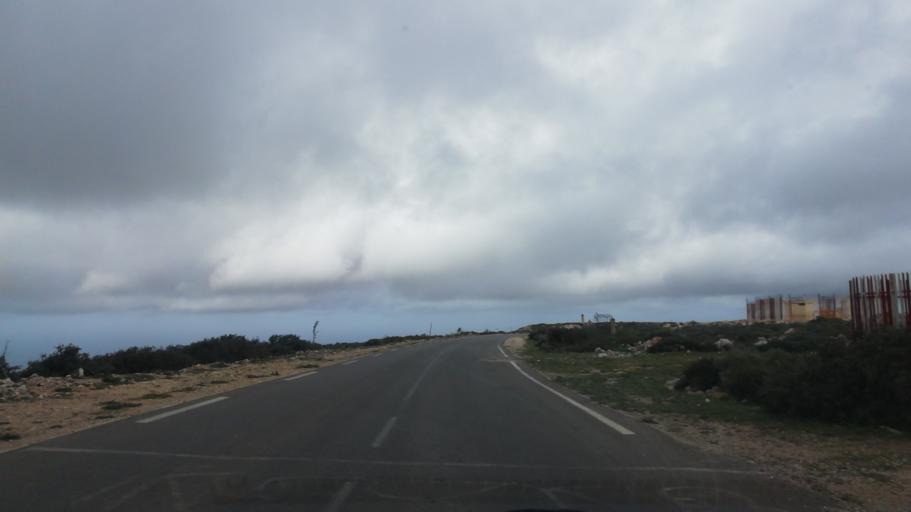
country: DZ
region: Oran
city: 'Ain el Turk
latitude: 35.6972
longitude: -0.7706
